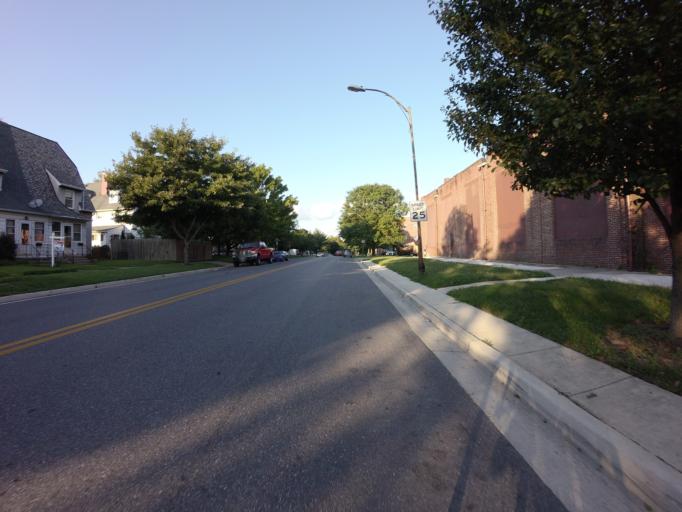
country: US
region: Maryland
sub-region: Baltimore County
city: Dundalk
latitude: 39.2590
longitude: -76.5231
